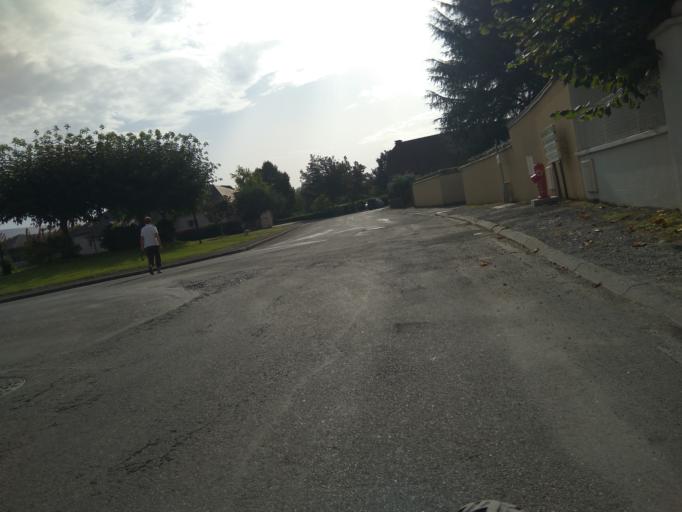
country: FR
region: Aquitaine
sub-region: Departement des Pyrenees-Atlantiques
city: Mazeres-Lezons
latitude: 43.2692
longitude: -0.3441
